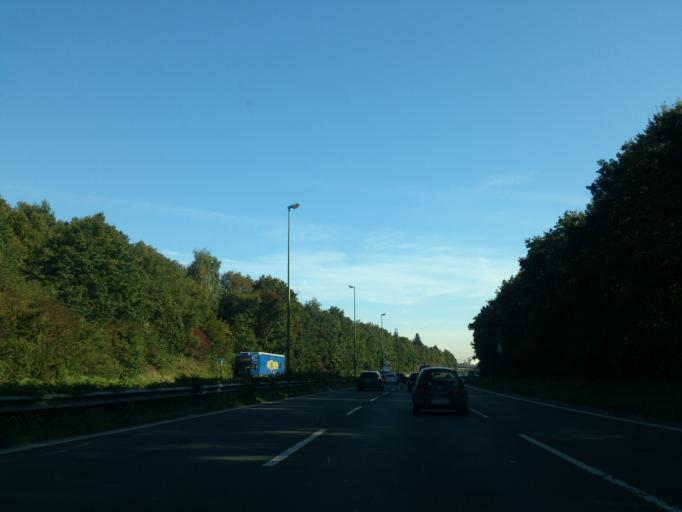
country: DE
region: North Rhine-Westphalia
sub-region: Regierungsbezirk Detmold
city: Bielefeld
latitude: 52.0062
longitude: 8.5048
